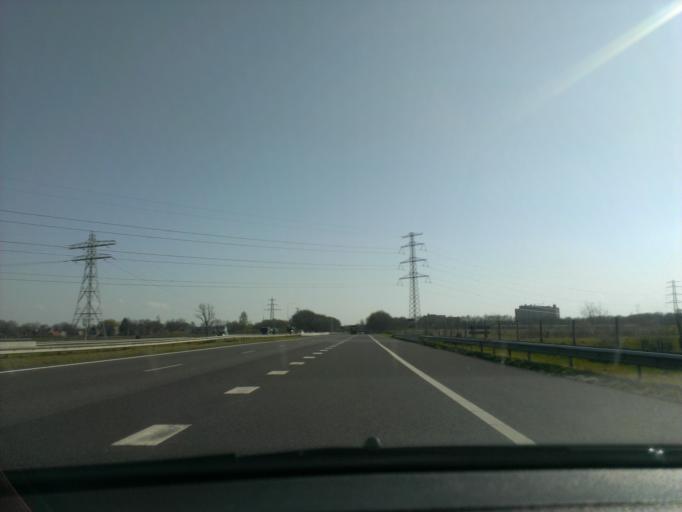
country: NL
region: Drenthe
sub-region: Gemeente Hoogeveen
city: Hoogeveen
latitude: 52.7347
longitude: 6.4651
